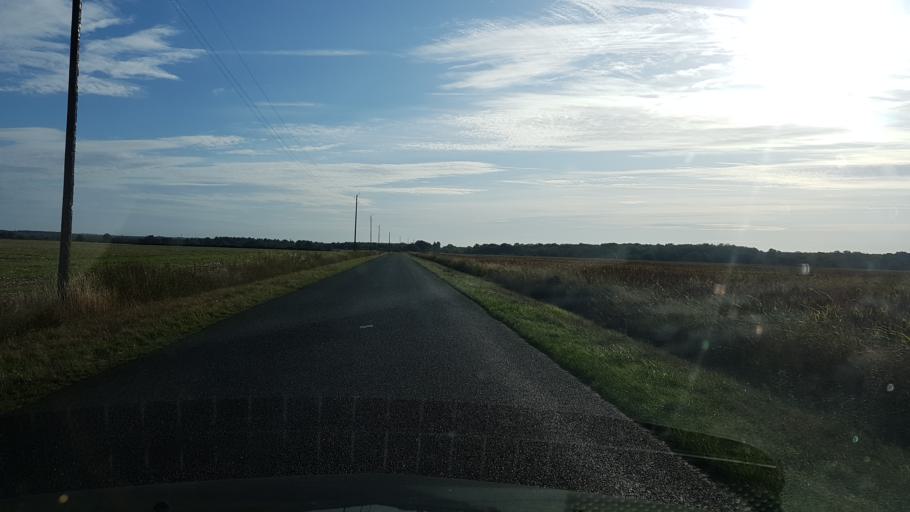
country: FR
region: Centre
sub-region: Departement du Loiret
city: Dampierre-en-Burly
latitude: 47.6960
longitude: 2.5086
